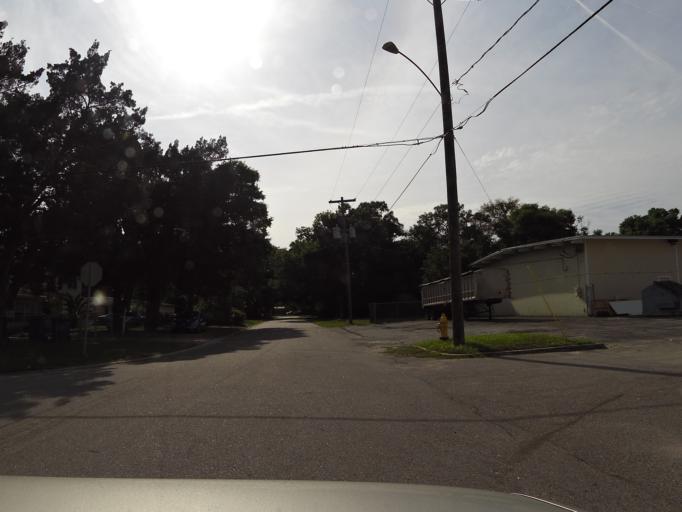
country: US
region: Florida
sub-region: Duval County
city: Jacksonville
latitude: 30.3325
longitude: -81.5899
